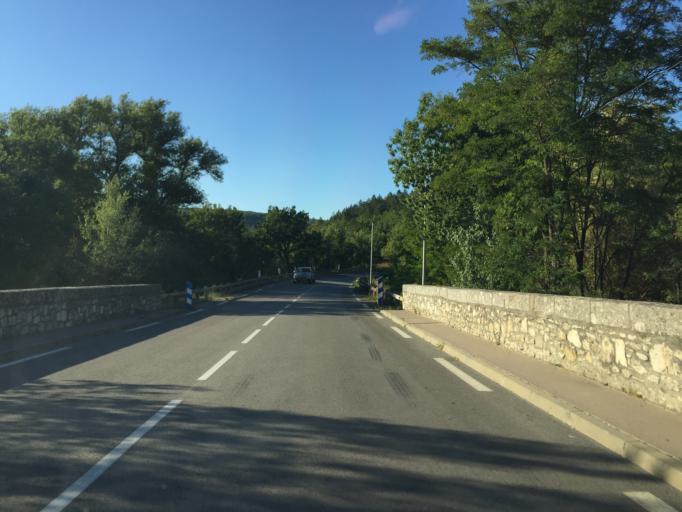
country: FR
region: Provence-Alpes-Cote d'Azur
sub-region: Departement des Alpes-de-Haute-Provence
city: Reillanne
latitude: 43.8789
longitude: 5.7034
